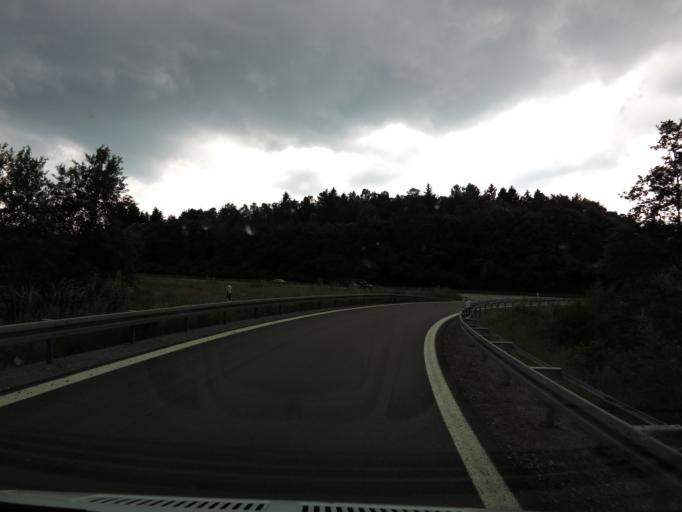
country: DE
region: Bavaria
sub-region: Lower Bavaria
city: Aicha vorm Wald
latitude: 48.6638
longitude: 13.2671
